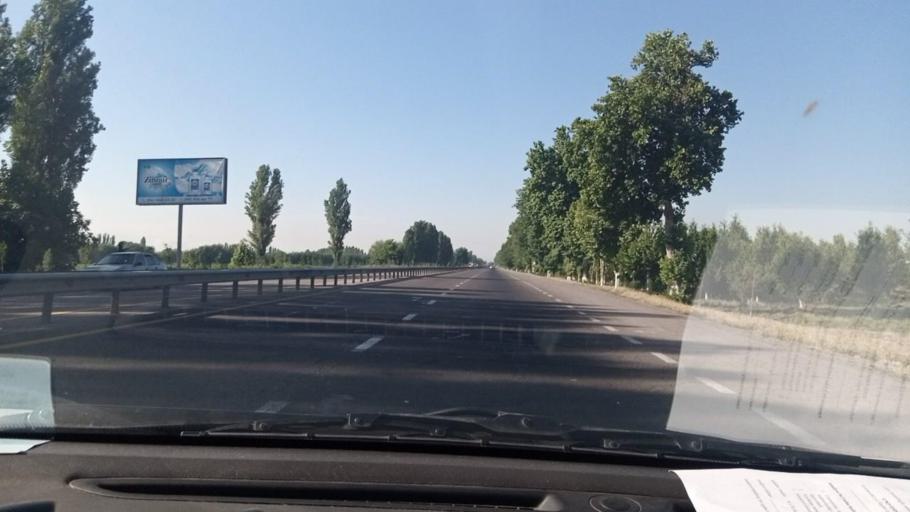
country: UZ
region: Toshkent Shahri
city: Bektemir
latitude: 41.2164
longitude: 69.4025
